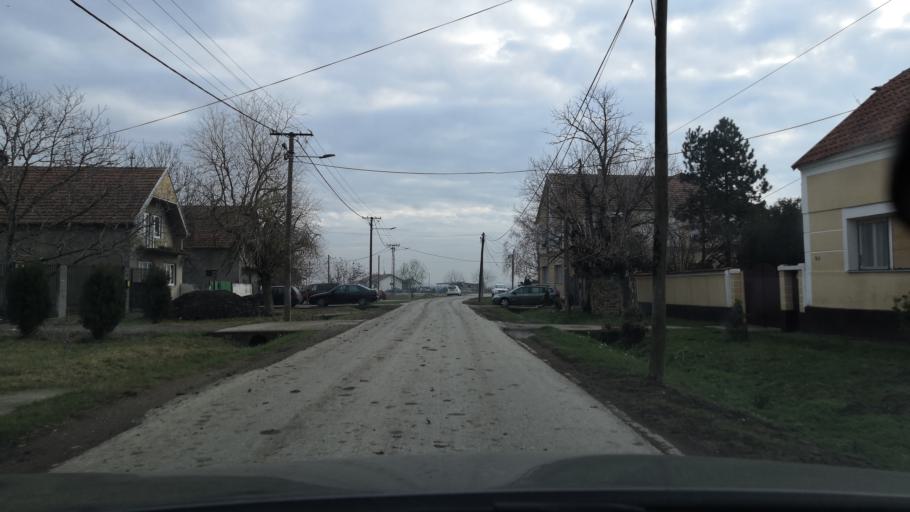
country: RS
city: Ugrinovci
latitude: 44.8875
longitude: 20.1450
